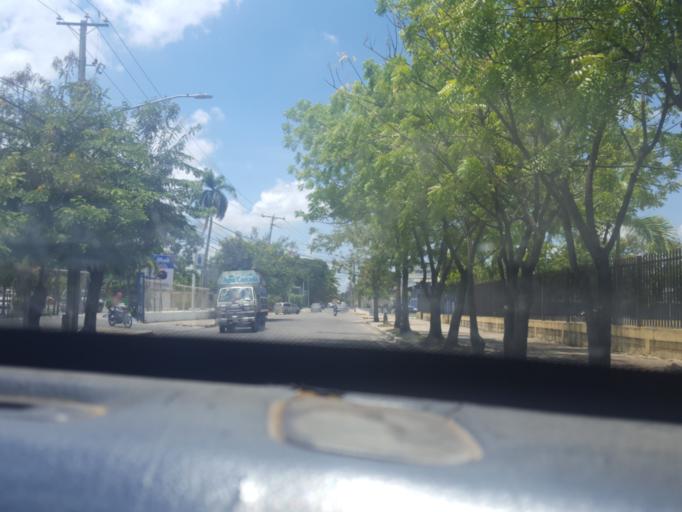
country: DO
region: Santiago
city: Santiago de los Caballeros
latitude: 19.4785
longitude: -70.7235
